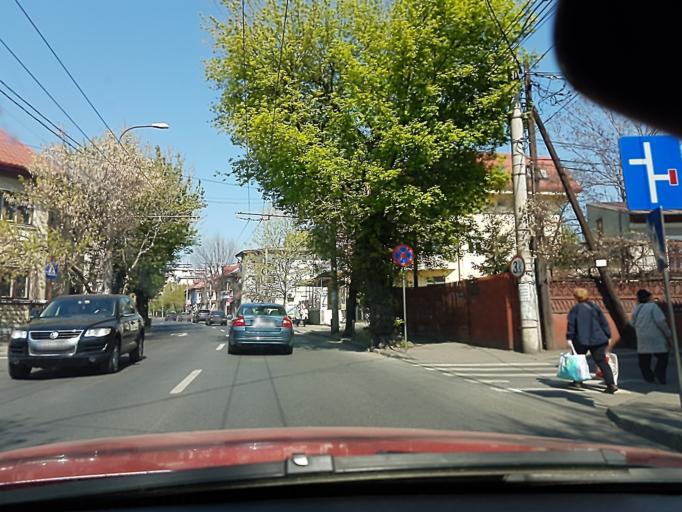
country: RO
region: Bucuresti
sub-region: Municipiul Bucuresti
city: Bucharest
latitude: 44.4258
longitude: 26.1361
